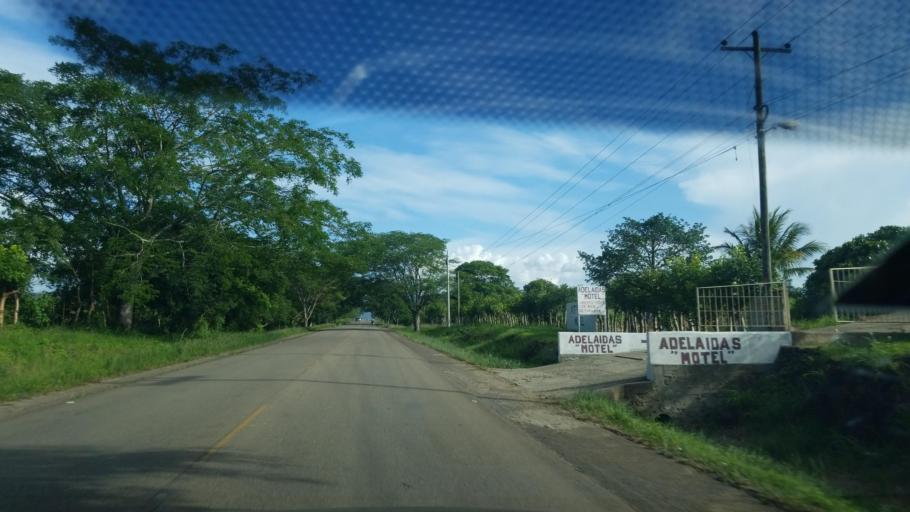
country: HN
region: El Paraiso
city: Arauli
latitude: 13.9217
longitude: -86.5578
